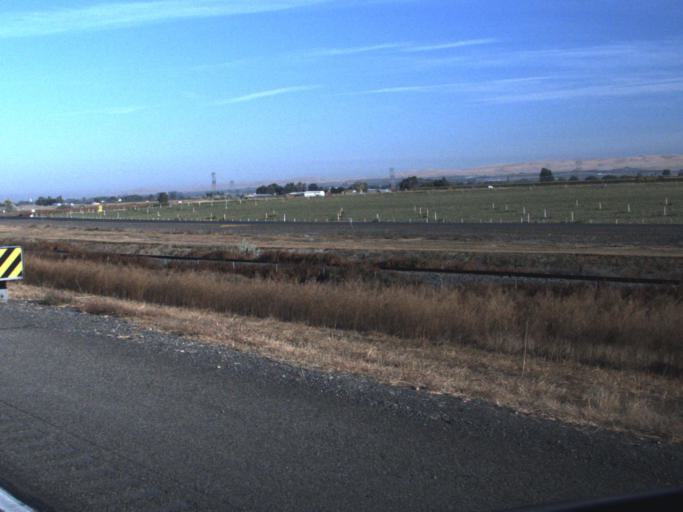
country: US
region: Washington
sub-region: Yakima County
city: Granger
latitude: 46.3320
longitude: -120.1210
